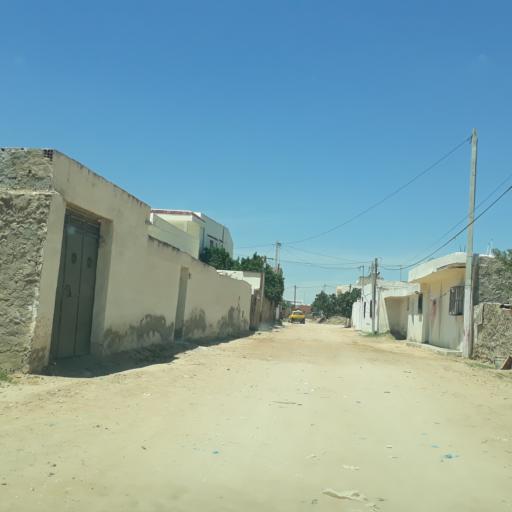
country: TN
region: Safaqis
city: Al Qarmadah
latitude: 34.8147
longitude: 10.7524
